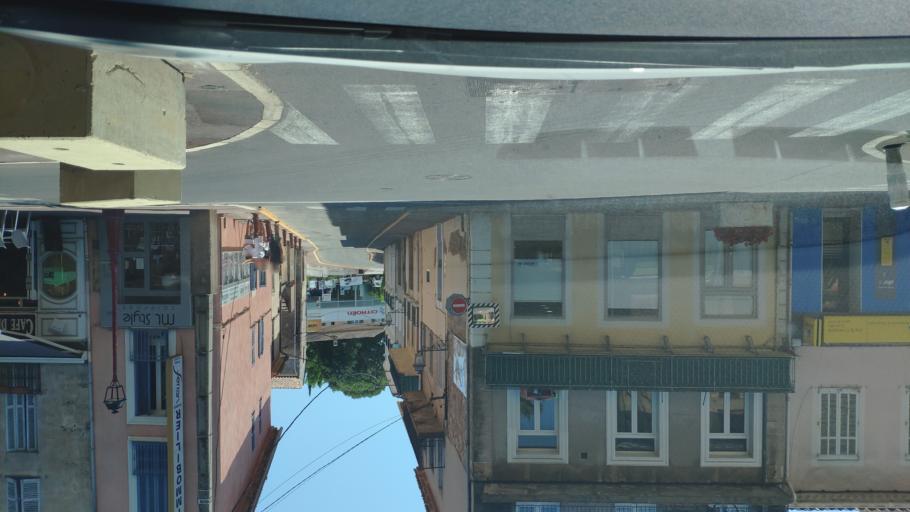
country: FR
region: Provence-Alpes-Cote d'Azur
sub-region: Departement du Var
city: Les Arcs
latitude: 43.4626
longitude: 6.4788
